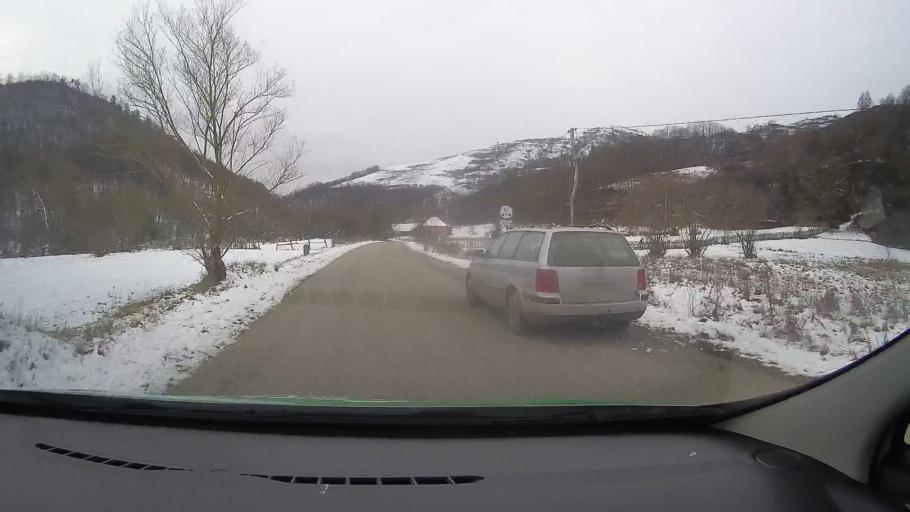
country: RO
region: Hunedoara
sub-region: Comuna Balsa
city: Balsa
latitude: 46.0613
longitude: 23.0984
